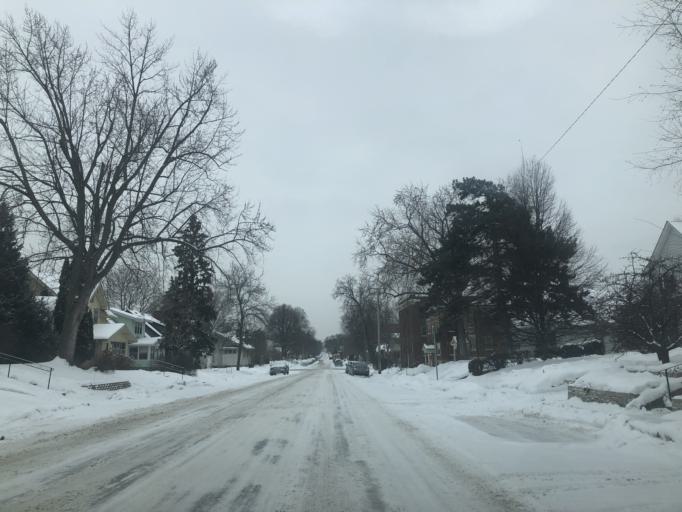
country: US
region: Minnesota
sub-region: Hennepin County
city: Richfield
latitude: 44.9279
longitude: -93.2909
